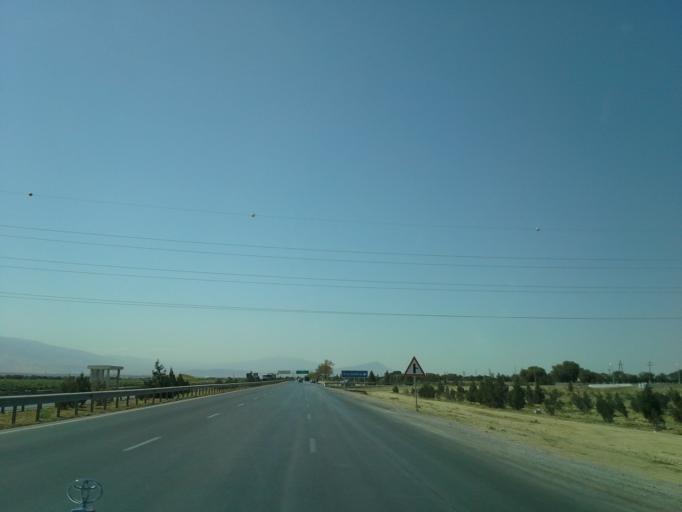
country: TM
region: Ahal
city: Annau
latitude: 37.9041
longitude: 58.5473
